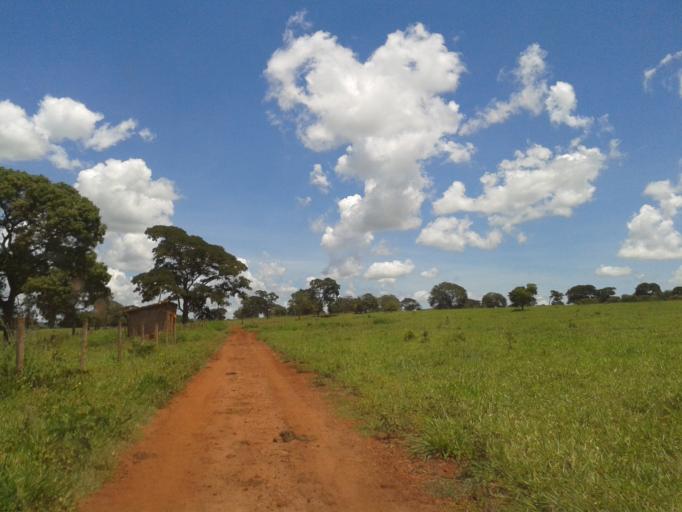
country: BR
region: Minas Gerais
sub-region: Santa Vitoria
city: Santa Vitoria
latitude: -18.7934
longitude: -49.8414
